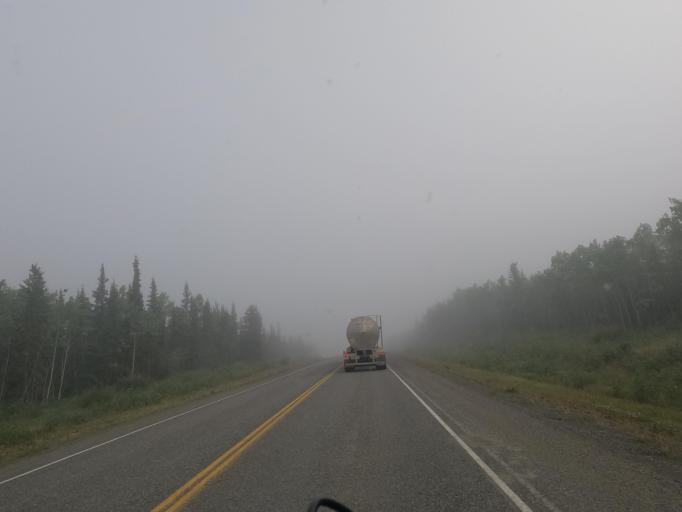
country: CA
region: Yukon
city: Whitehorse
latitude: 61.1181
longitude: -135.3304
